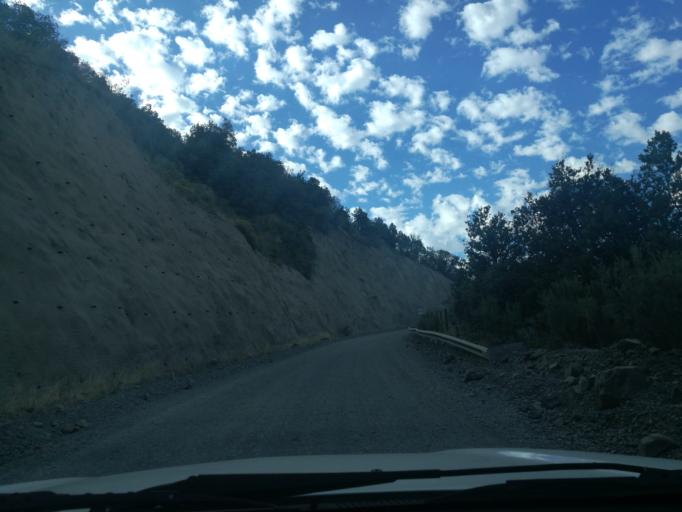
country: CL
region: O'Higgins
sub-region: Provincia de Cachapoal
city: Machali
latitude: -34.2855
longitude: -70.4382
